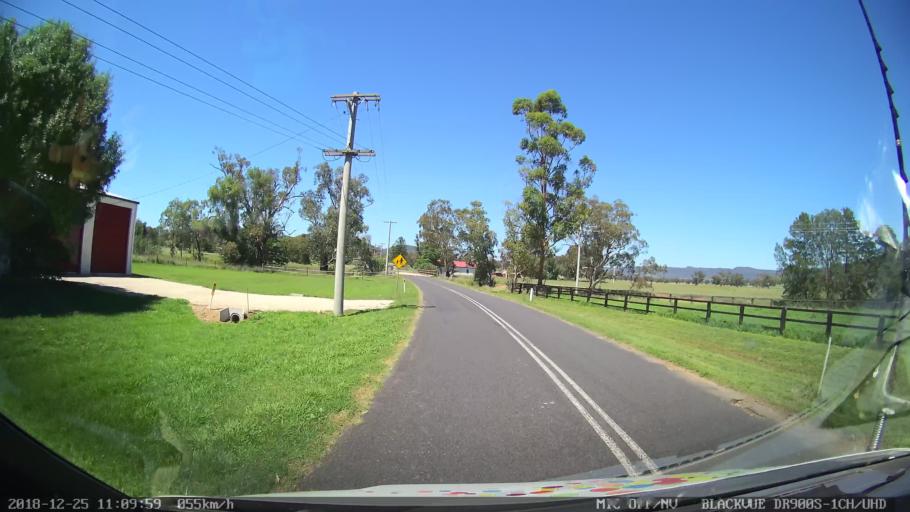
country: AU
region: New South Wales
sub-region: Upper Hunter Shire
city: Merriwa
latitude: -32.4145
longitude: 150.1160
